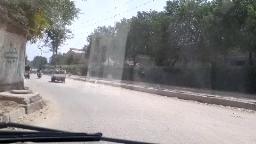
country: PK
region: Sindh
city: Malir Cantonment
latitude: 24.8405
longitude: 67.2042
